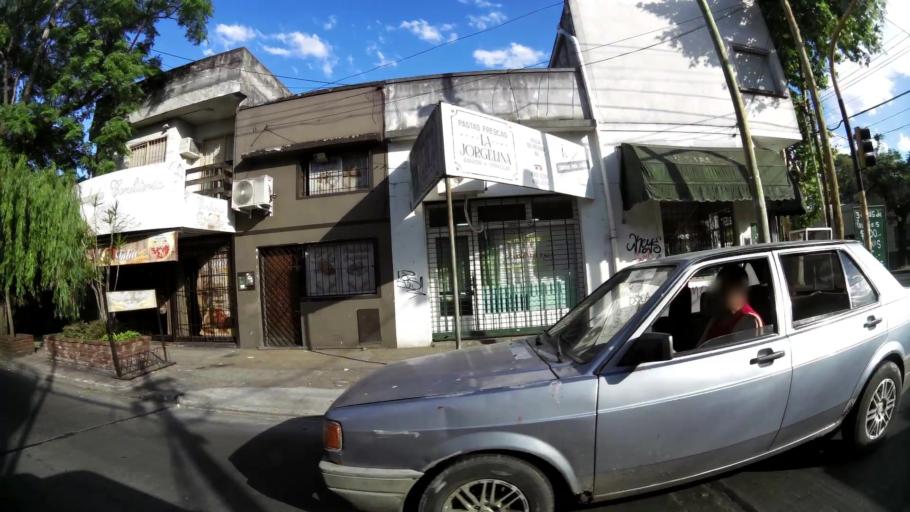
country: AR
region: Buenos Aires
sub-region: Partido de General San Martin
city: General San Martin
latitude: -34.5402
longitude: -58.5656
